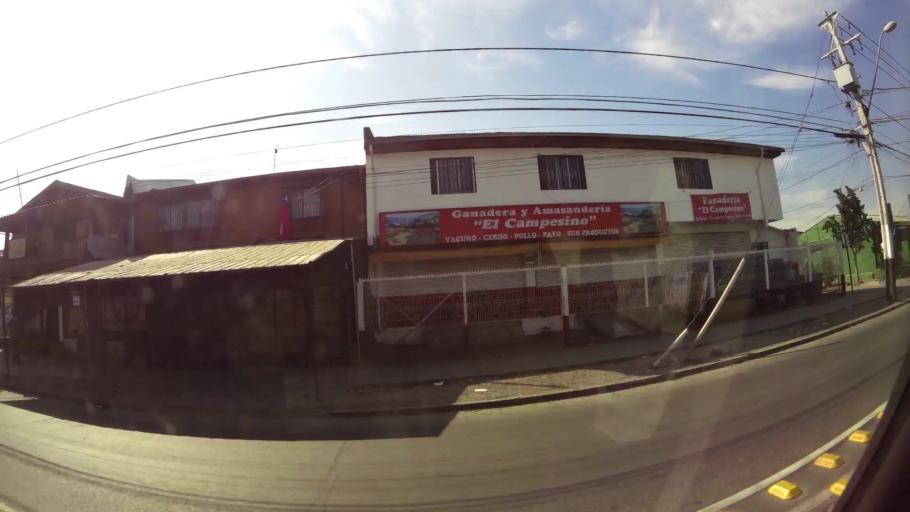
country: CL
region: Santiago Metropolitan
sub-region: Provincia de Santiago
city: Lo Prado
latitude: -33.4450
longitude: -70.7539
